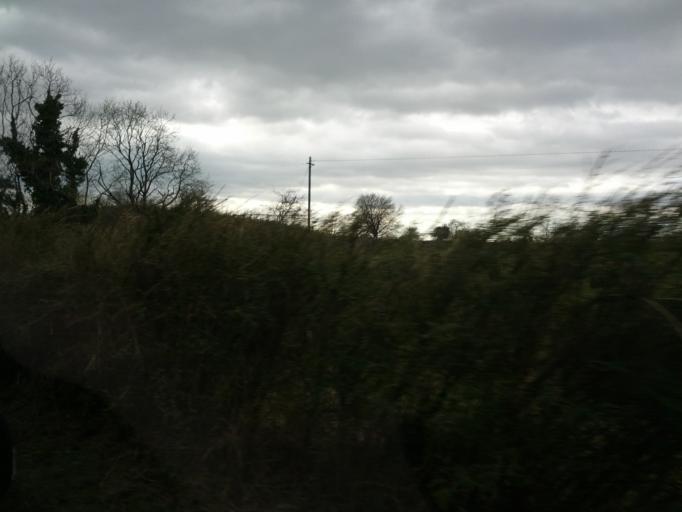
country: IE
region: Connaught
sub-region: County Galway
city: Athenry
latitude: 53.3821
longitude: -8.6241
